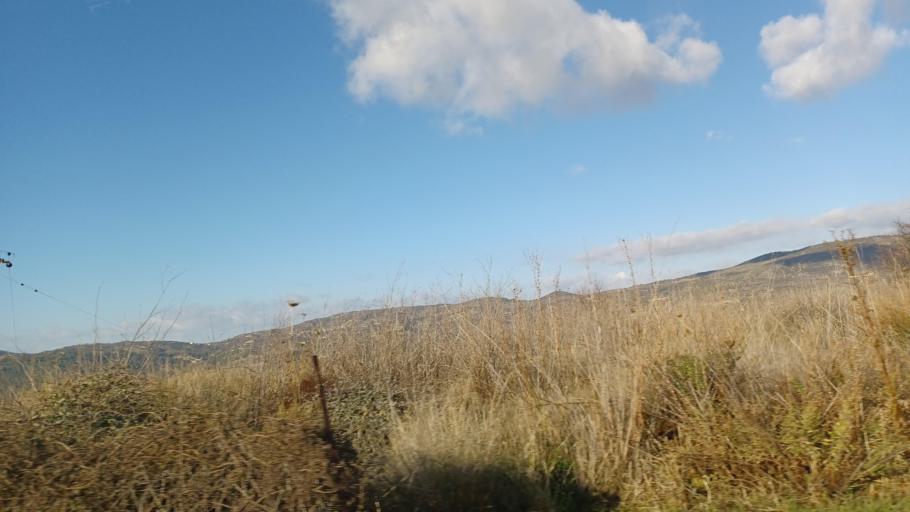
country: CY
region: Limassol
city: Pachna
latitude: 34.8448
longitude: 32.7388
